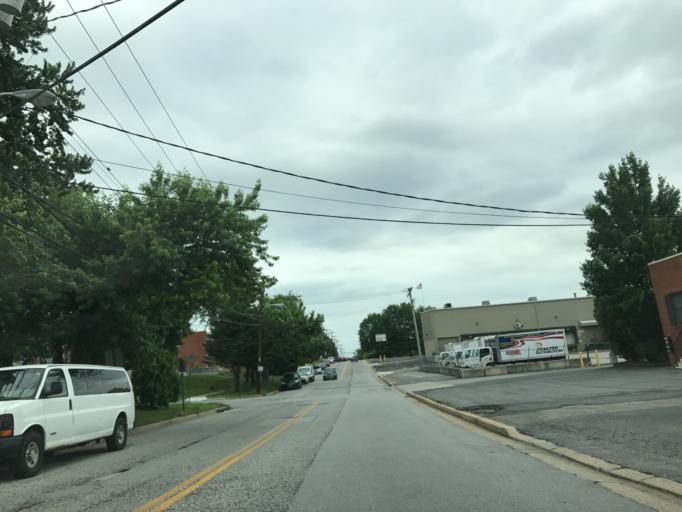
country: US
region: Maryland
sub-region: Baltimore County
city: Lansdowne
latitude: 39.2651
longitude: -76.6741
